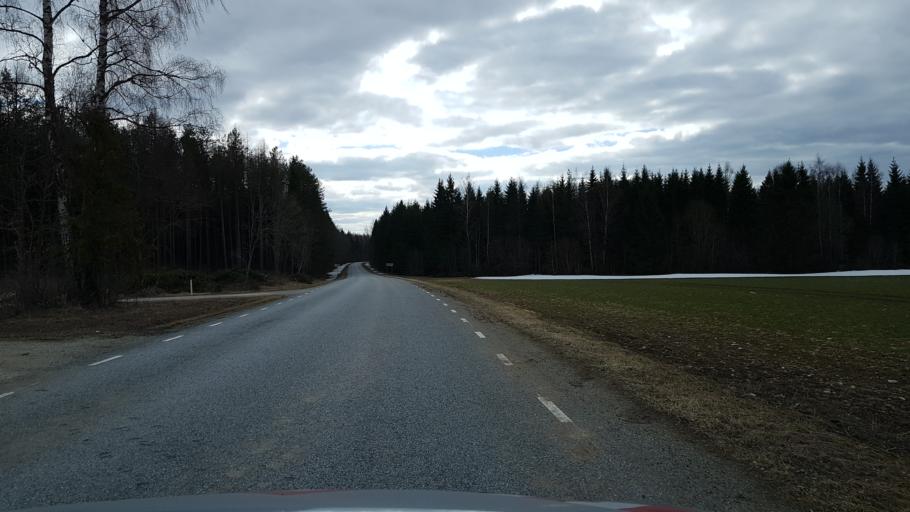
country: EE
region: Laeaene-Virumaa
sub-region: Tamsalu vald
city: Tamsalu
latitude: 59.2204
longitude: 26.1609
